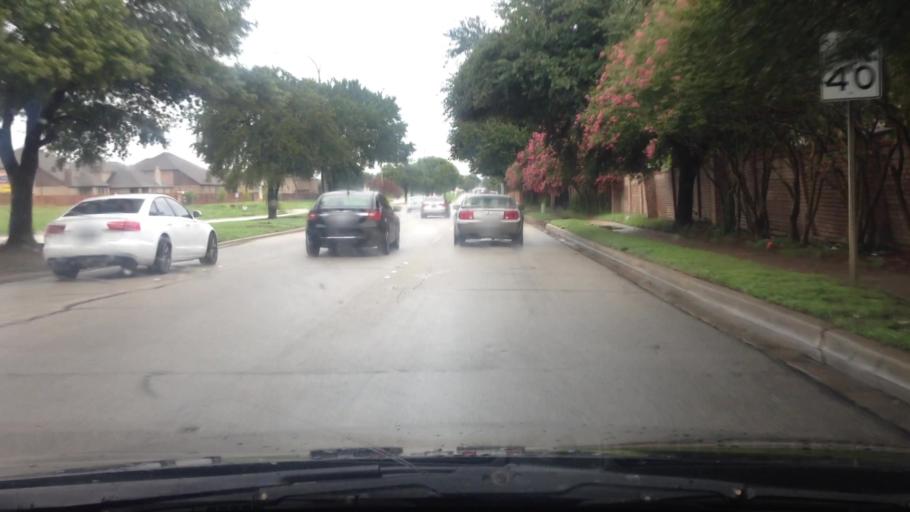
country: US
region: Texas
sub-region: Tarrant County
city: Watauga
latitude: 32.8500
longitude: -97.2899
